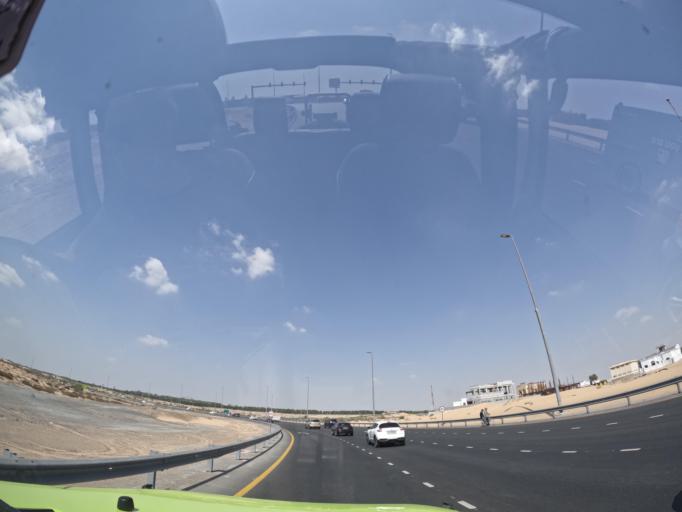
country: AE
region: Ash Shariqah
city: Sharjah
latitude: 25.1686
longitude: 55.4621
